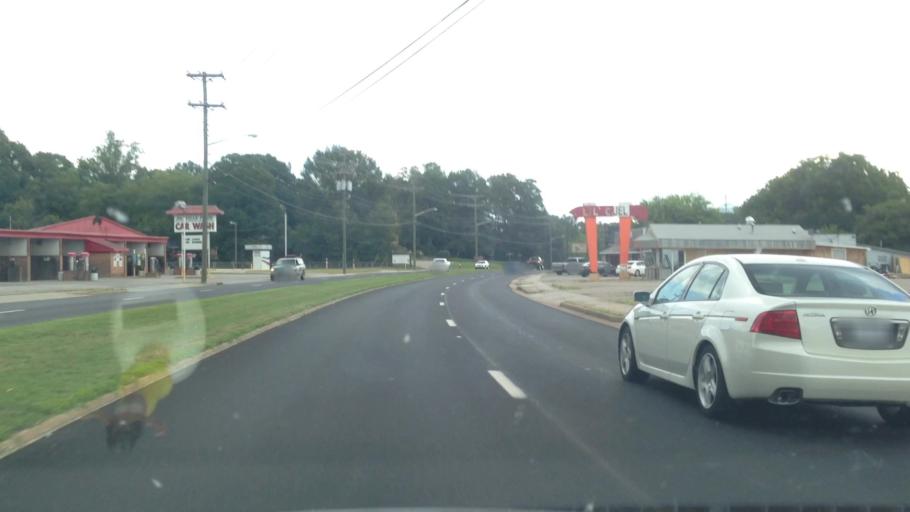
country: US
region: Virginia
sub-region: City of Danville
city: Danville
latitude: 36.5631
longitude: -79.4507
